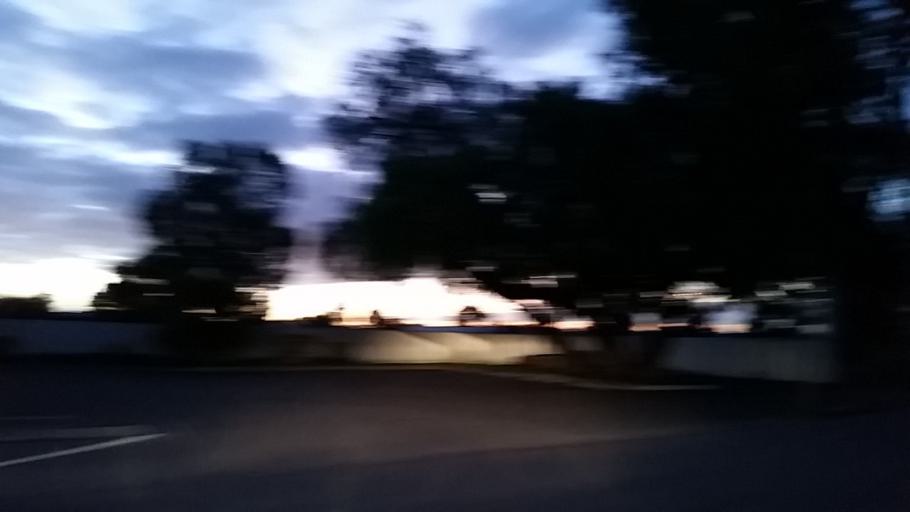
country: AU
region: South Australia
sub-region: Gawler
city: Gawler
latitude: -34.6069
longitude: 138.7401
